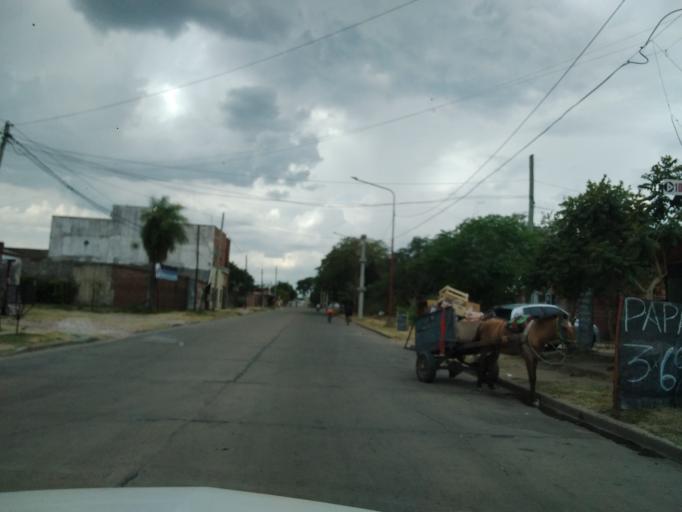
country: AR
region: Corrientes
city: Corrientes
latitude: -27.5248
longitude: -58.7958
